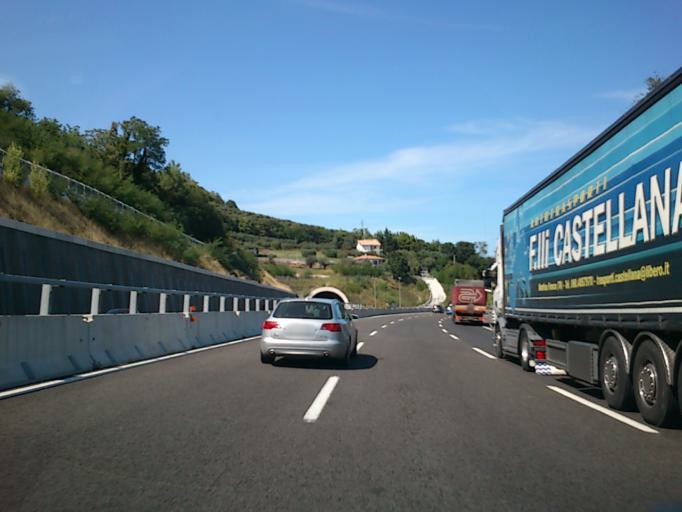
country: IT
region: The Marches
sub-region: Provincia di Pesaro e Urbino
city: Fenile
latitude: 43.8600
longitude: 12.9372
